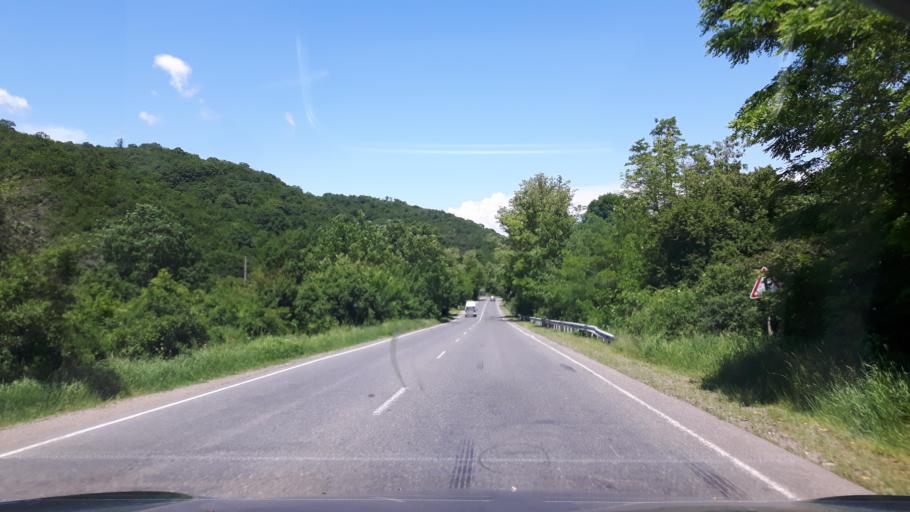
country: GE
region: Kakheti
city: Sighnaghi
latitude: 41.6382
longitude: 45.8271
